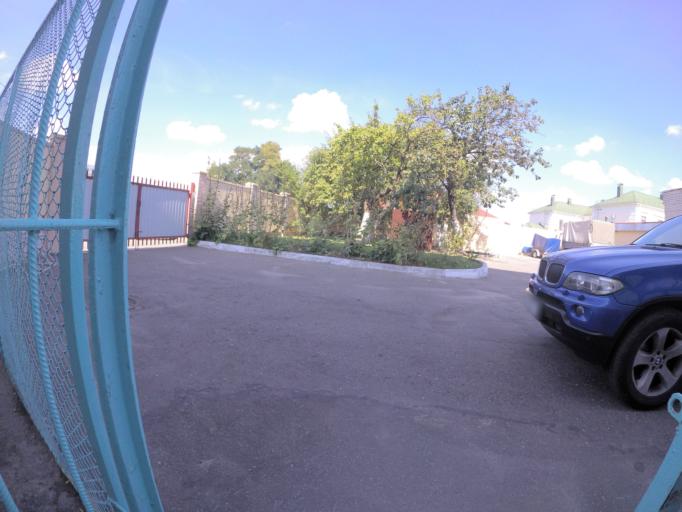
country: BY
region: Grodnenskaya
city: Hrodna
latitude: 53.6741
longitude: 23.8396
